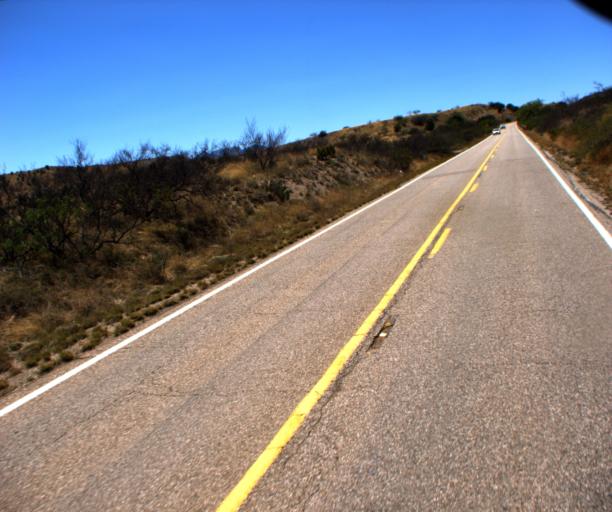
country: US
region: Arizona
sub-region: Pima County
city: Corona de Tucson
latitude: 31.8327
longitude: -110.7035
